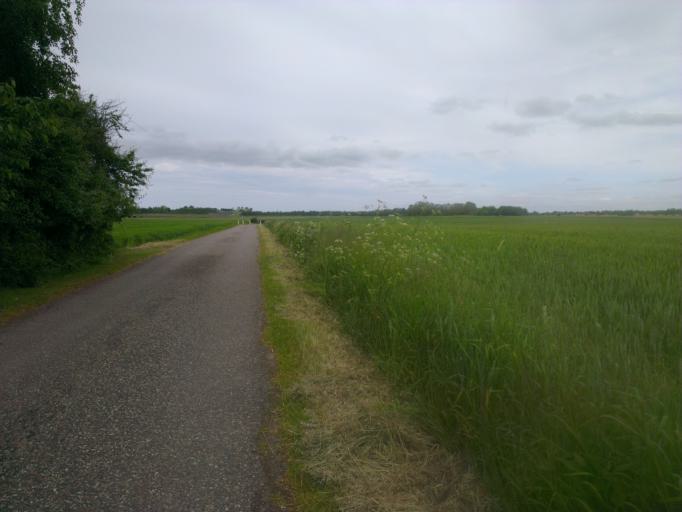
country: DK
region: Capital Region
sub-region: Frederikssund Kommune
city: Frederikssund
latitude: 55.8081
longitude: 12.0770
